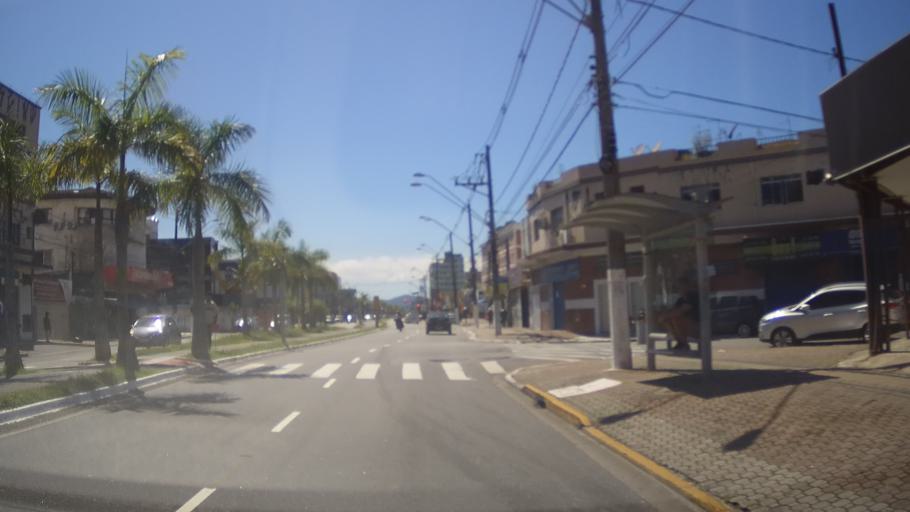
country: BR
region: Sao Paulo
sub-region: Praia Grande
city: Praia Grande
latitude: -24.0204
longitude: -46.4646
